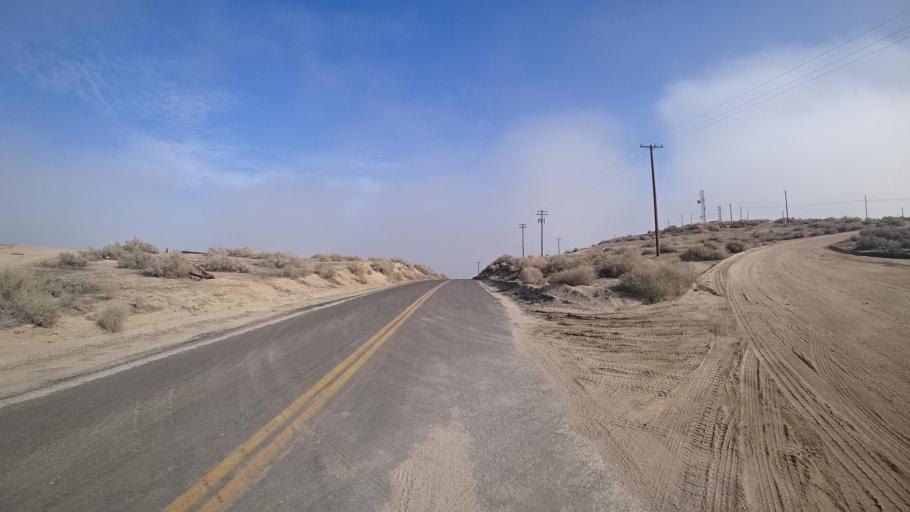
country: US
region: California
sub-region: Kern County
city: Ford City
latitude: 35.1659
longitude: -119.4113
